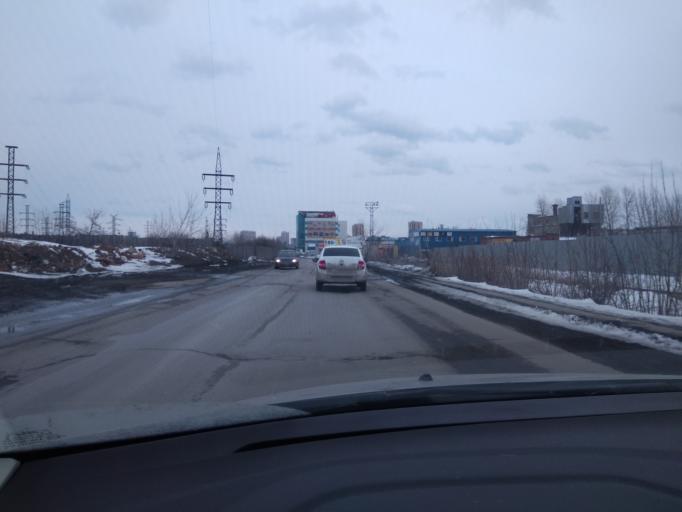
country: RU
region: Sverdlovsk
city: Yekaterinburg
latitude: 56.8757
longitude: 60.6280
